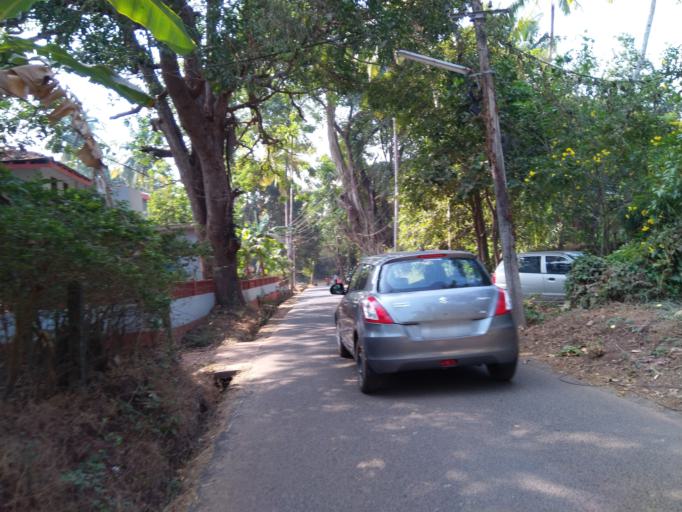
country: IN
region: Goa
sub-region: North Goa
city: Saligao
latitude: 15.5643
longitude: 73.7689
